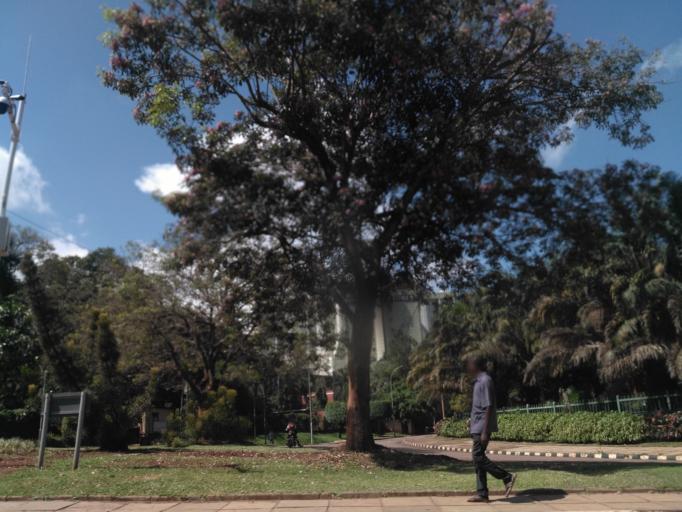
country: UG
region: Central Region
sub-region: Kampala District
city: Kampala
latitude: 0.3169
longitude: 32.5858
